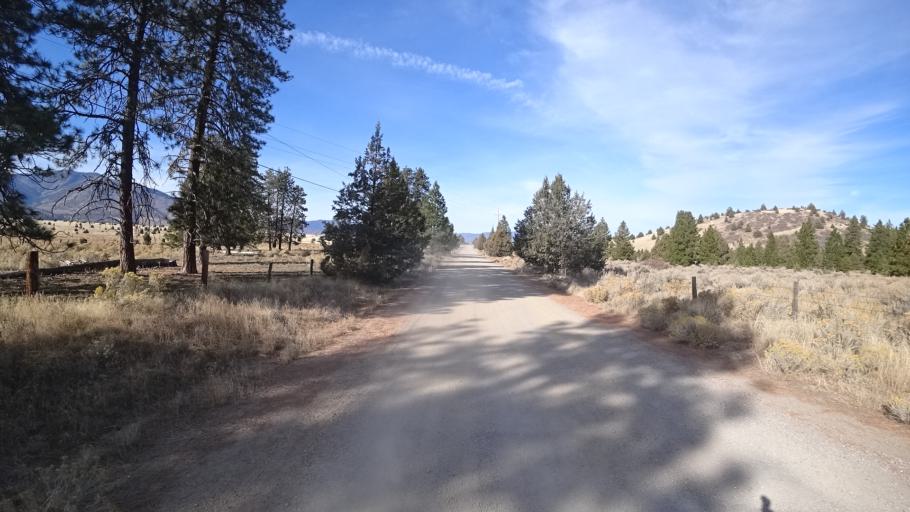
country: US
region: California
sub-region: Siskiyou County
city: Weed
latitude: 41.4873
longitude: -122.4437
